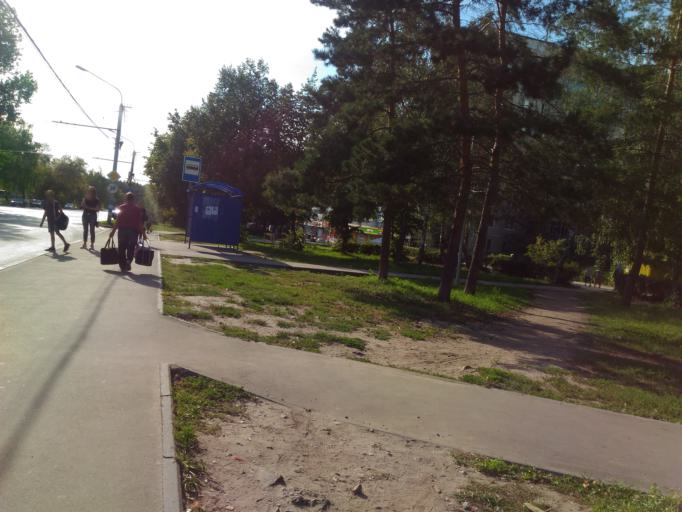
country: RU
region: Ulyanovsk
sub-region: Ulyanovskiy Rayon
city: Ulyanovsk
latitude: 54.3530
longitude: 48.5338
